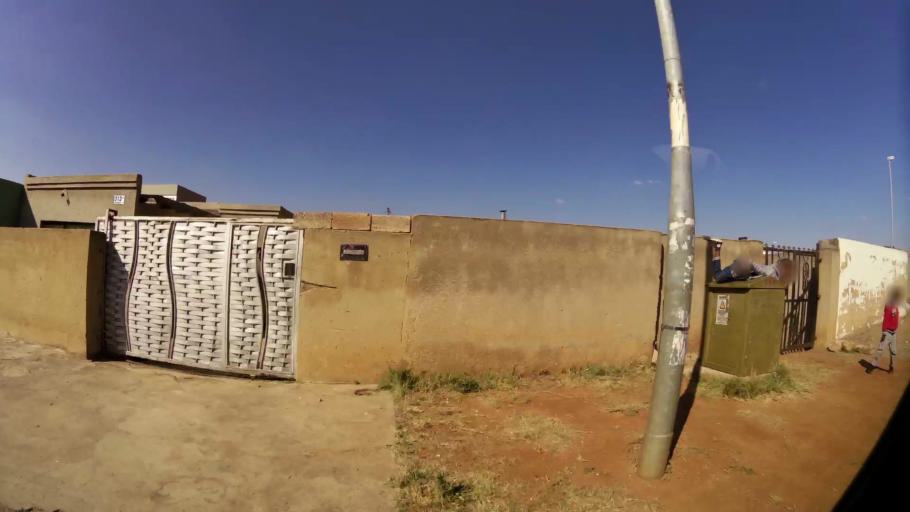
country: ZA
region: Gauteng
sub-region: City of Johannesburg Metropolitan Municipality
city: Soweto
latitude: -26.2314
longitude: 27.8831
